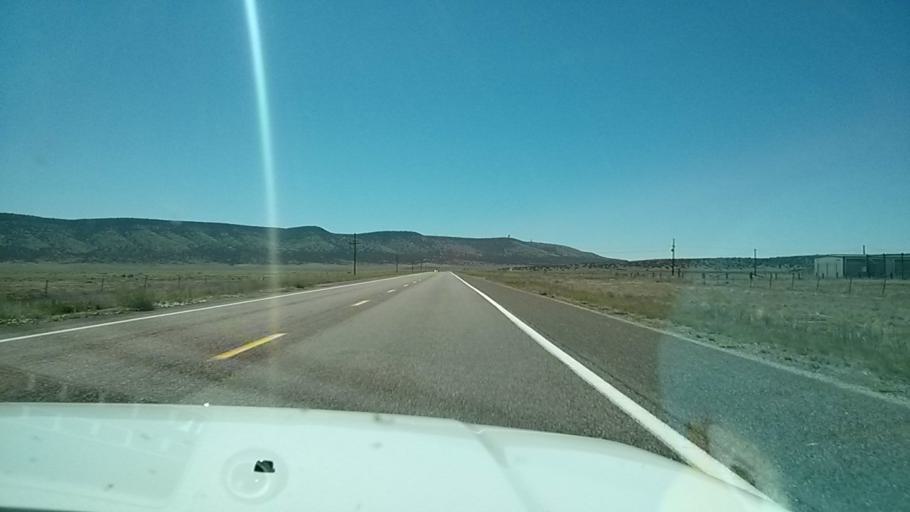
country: US
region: Arizona
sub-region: Mohave County
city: Peach Springs
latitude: 35.3922
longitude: -113.0028
